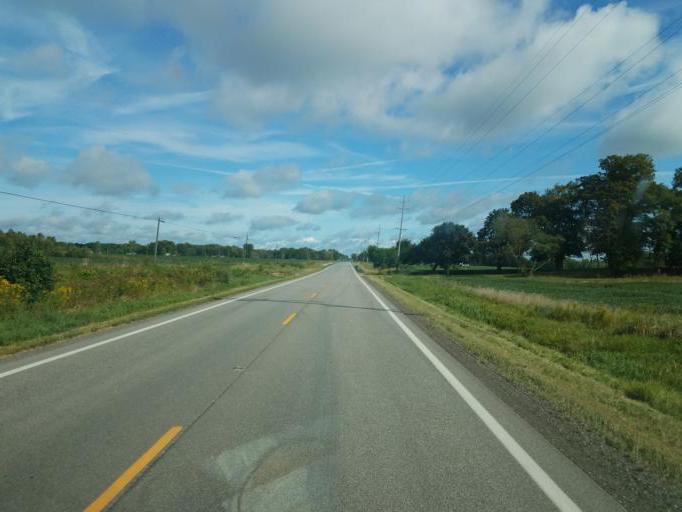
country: US
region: Ohio
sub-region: Wayne County
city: West Salem
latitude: 41.0783
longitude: -82.1237
